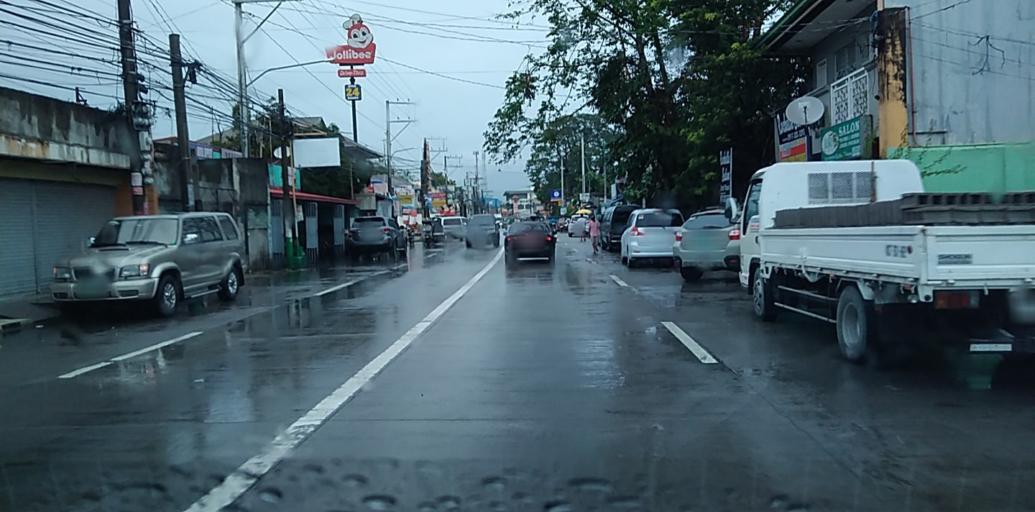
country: PH
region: Central Luzon
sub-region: Province of Pampanga
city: Mexico
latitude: 15.0621
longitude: 120.7200
